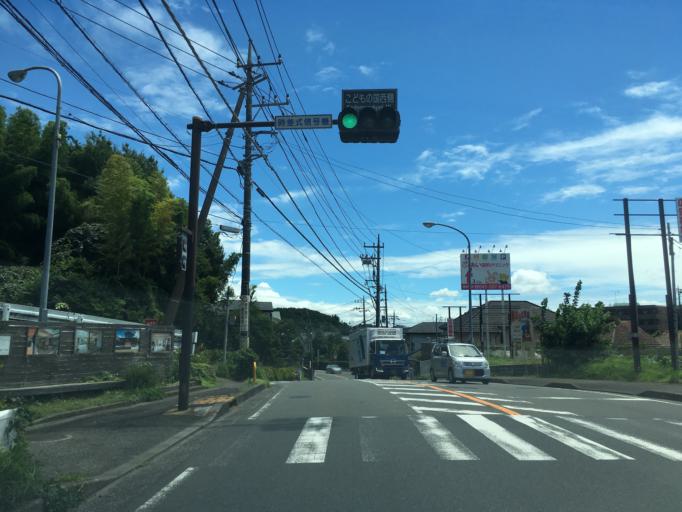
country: JP
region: Tokyo
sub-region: Machida-shi
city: Machida
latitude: 35.5615
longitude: 139.4840
